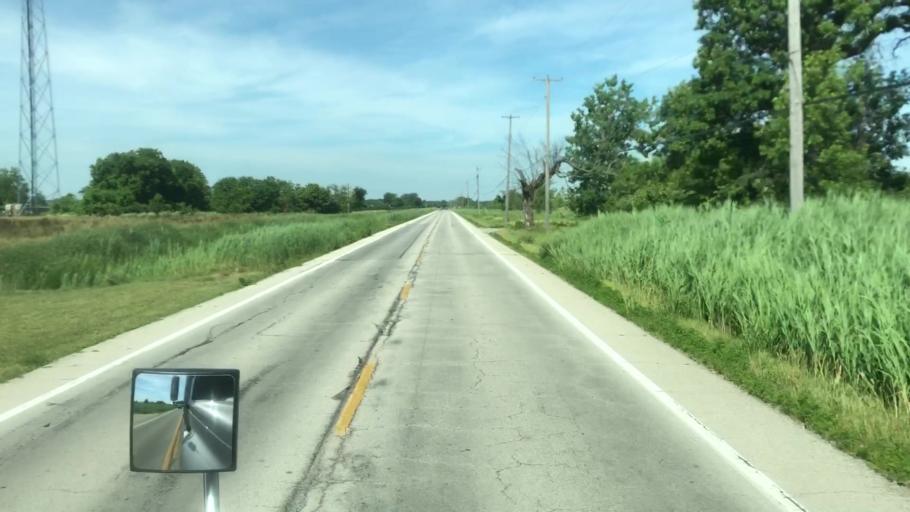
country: US
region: Ohio
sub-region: Ottawa County
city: Port Clinton
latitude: 41.4086
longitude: -82.9201
